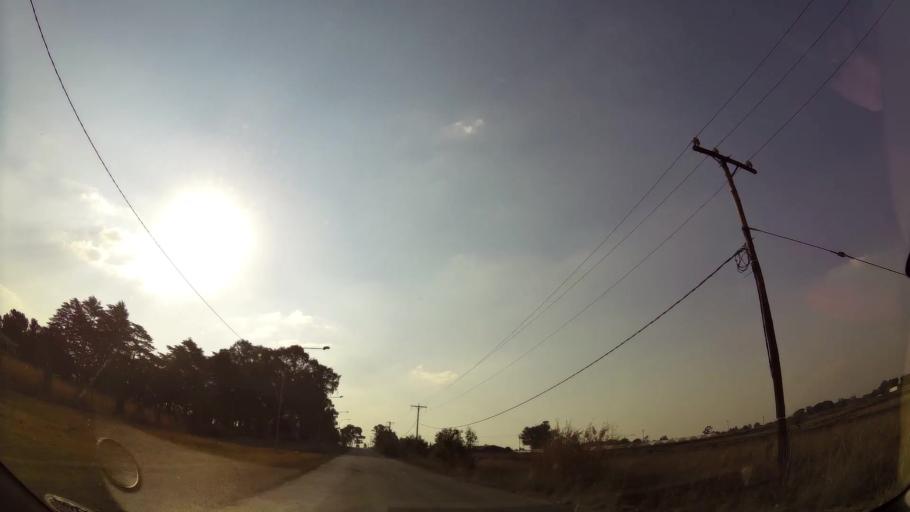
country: ZA
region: Gauteng
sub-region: Ekurhuleni Metropolitan Municipality
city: Benoni
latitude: -26.1108
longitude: 28.3870
